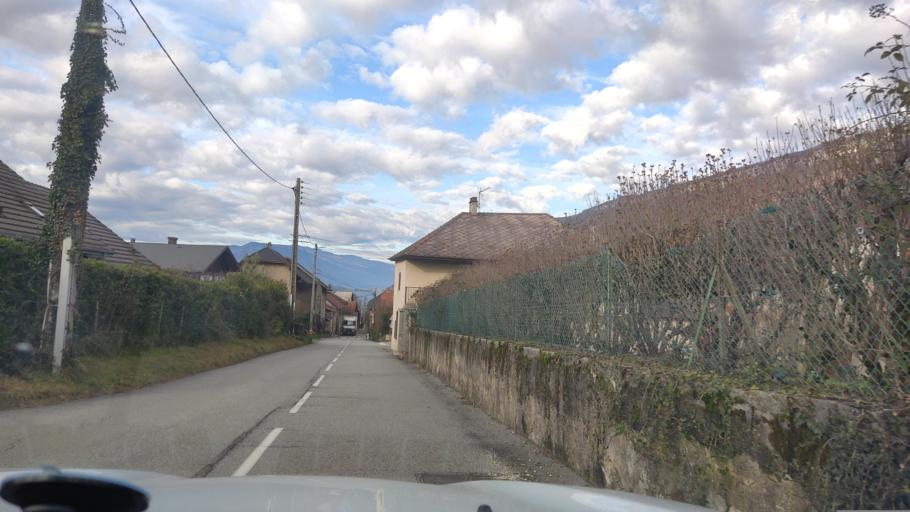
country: FR
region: Rhone-Alpes
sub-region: Departement de la Savoie
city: Brison-Saint-Innocent
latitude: 45.7290
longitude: 5.8866
